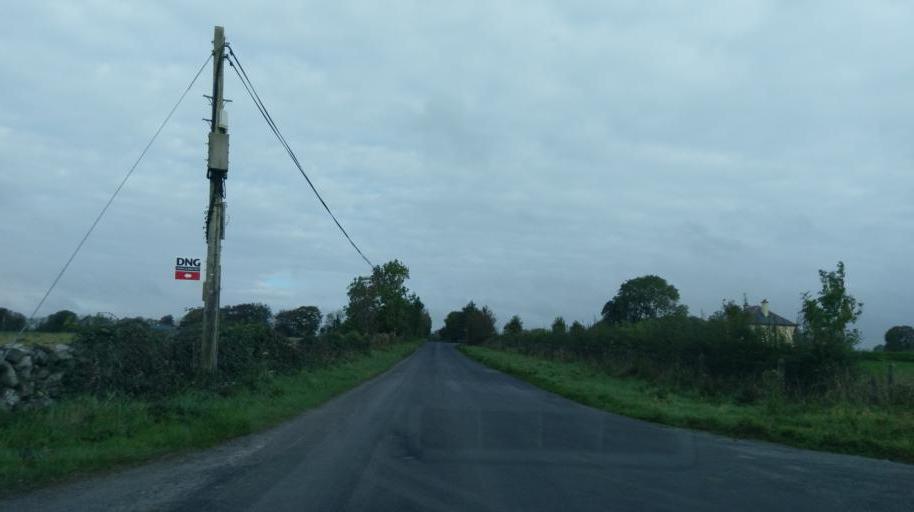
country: IE
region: Connaught
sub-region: County Galway
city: Athenry
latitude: 53.4310
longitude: -8.6399
